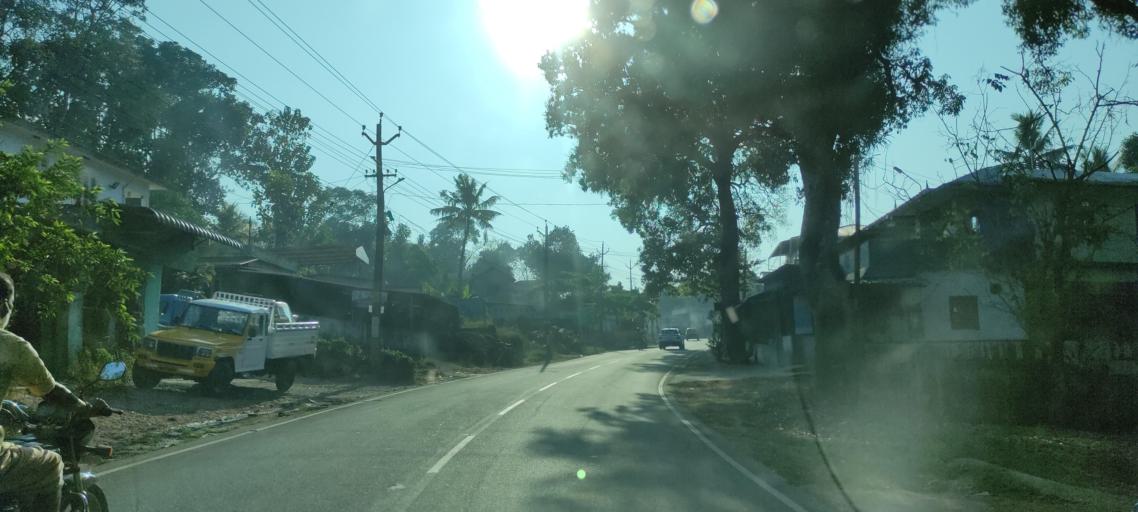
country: IN
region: Kerala
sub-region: Pattanamtitta
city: Adur
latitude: 9.1680
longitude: 76.6622
